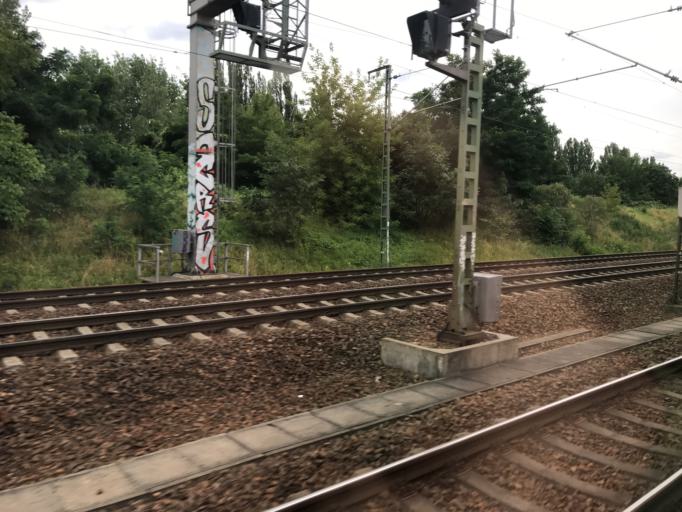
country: DE
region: Berlin
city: Pankow
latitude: 52.5616
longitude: 13.4022
